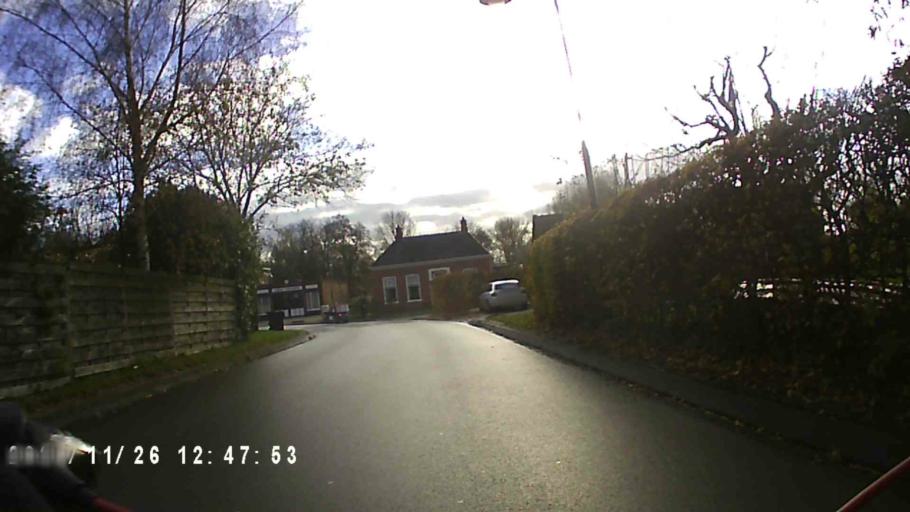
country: NL
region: Groningen
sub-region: Gemeente Appingedam
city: Appingedam
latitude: 53.3480
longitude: 6.7624
